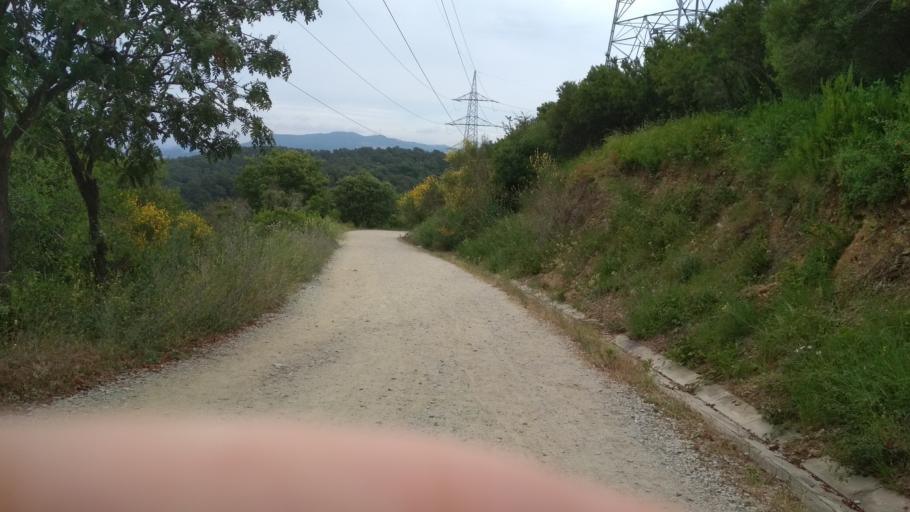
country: ES
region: Catalonia
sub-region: Provincia de Barcelona
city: Nou Barris
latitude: 41.4501
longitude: 2.1577
